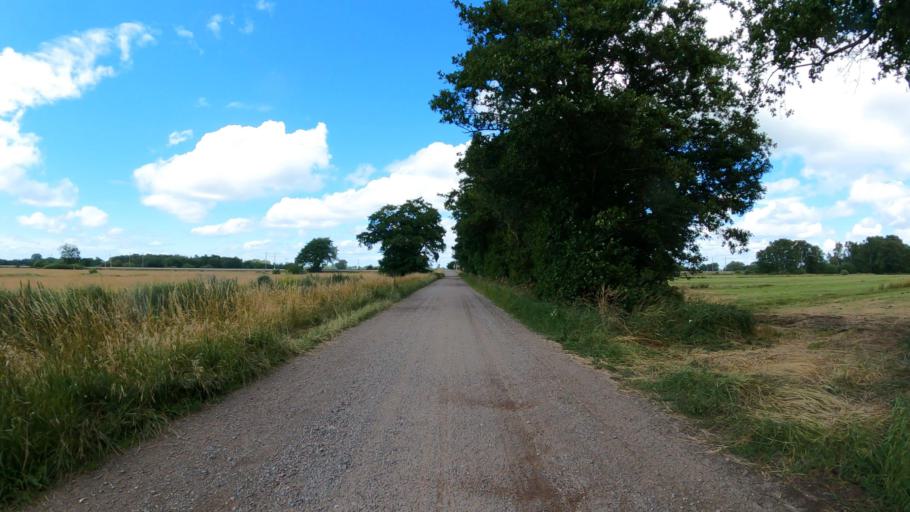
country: DE
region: Lower Saxony
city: Neu Wulmstorf
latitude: 53.4696
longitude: 9.7580
